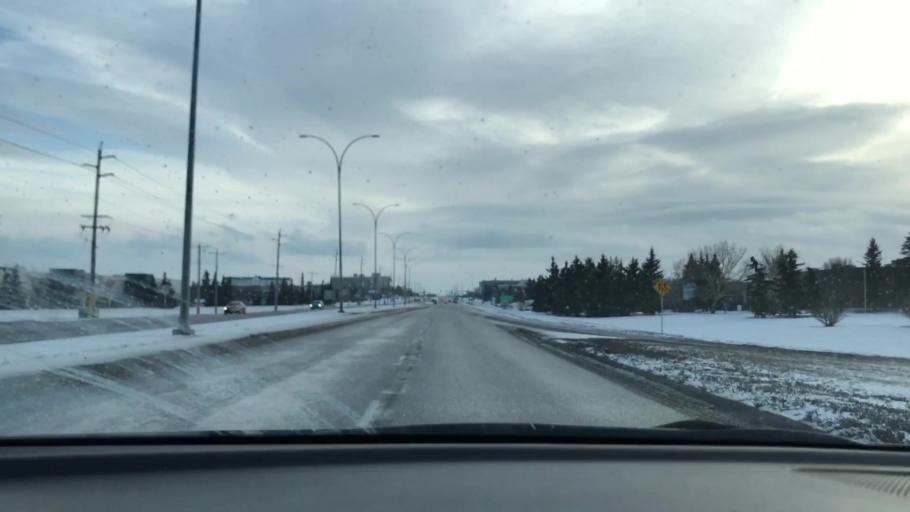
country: CA
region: Alberta
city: Calgary
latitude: 51.0923
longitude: -114.0019
